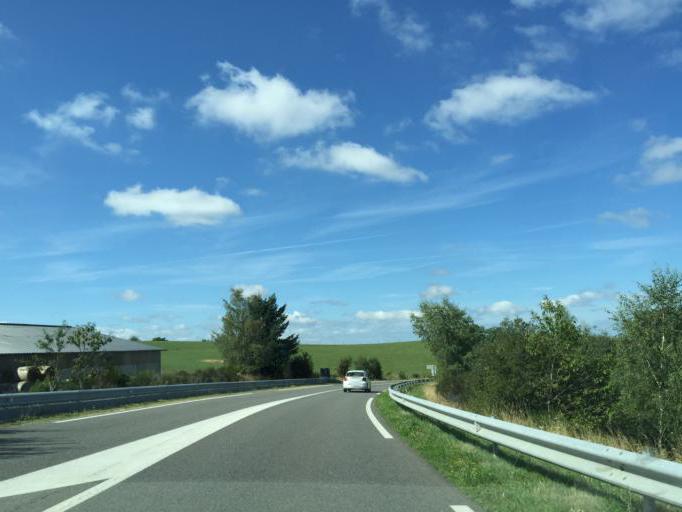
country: FR
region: Midi-Pyrenees
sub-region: Departement de l'Aveyron
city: Rieupeyroux
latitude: 44.3074
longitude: 2.1732
